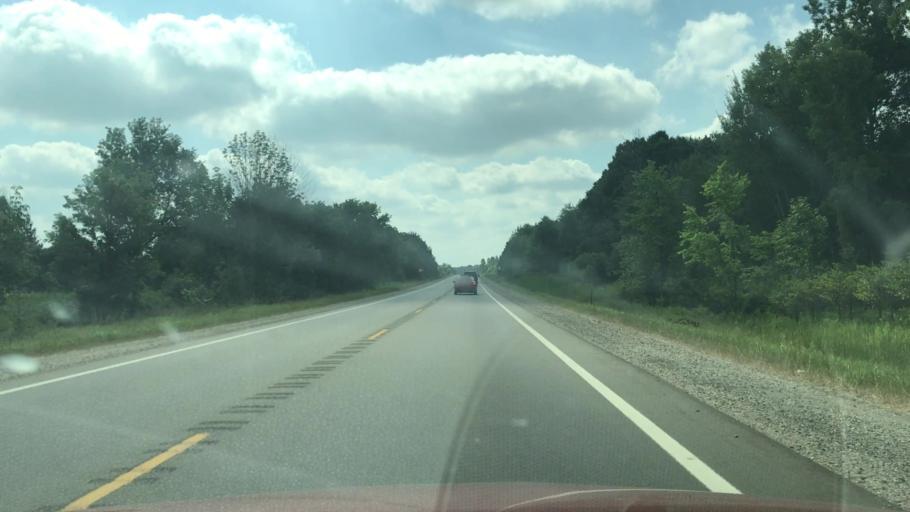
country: US
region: Michigan
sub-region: Kent County
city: Kent City
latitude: 43.2092
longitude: -85.7457
